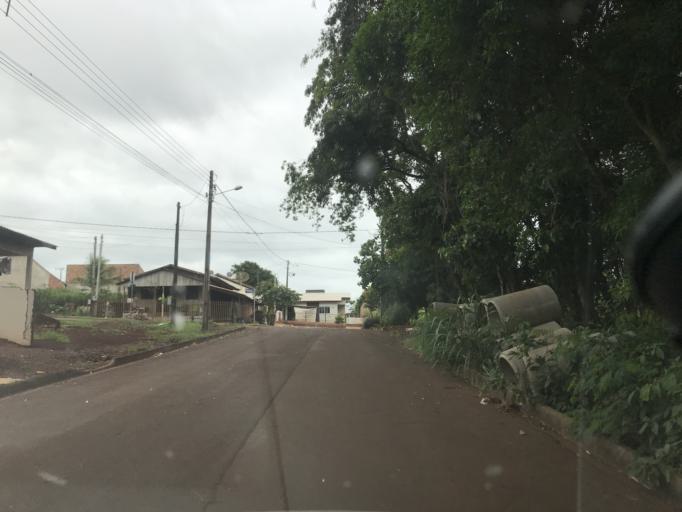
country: BR
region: Parana
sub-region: Palotina
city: Palotina
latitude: -24.3008
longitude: -53.8298
